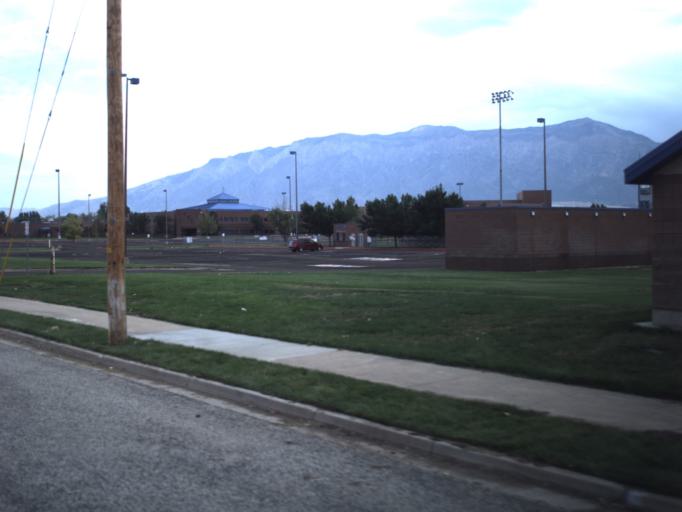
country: US
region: Utah
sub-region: Weber County
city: Plain City
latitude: 41.2897
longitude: -112.0932
